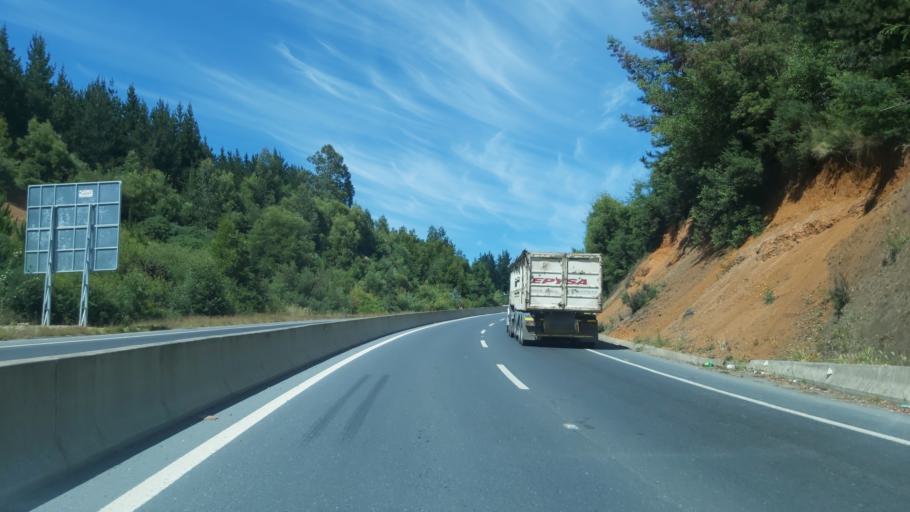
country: CL
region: Biobio
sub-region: Provincia de Concepcion
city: Lota
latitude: -37.0821
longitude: -73.1372
